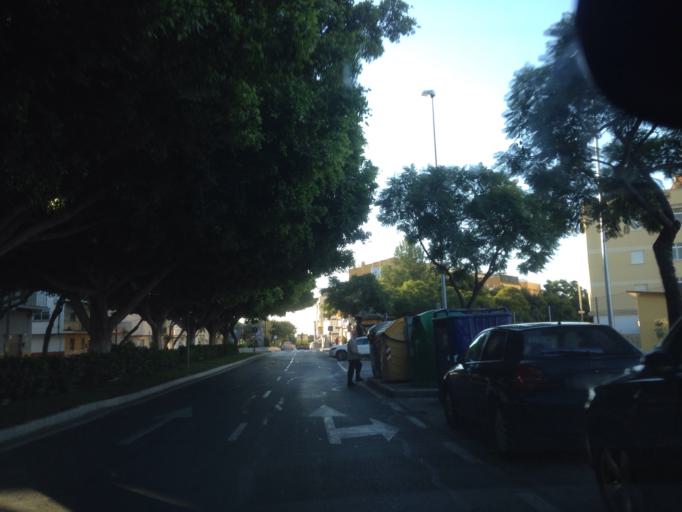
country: ES
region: Andalusia
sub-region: Provincia de Malaga
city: Malaga
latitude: 36.7225
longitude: -4.4726
